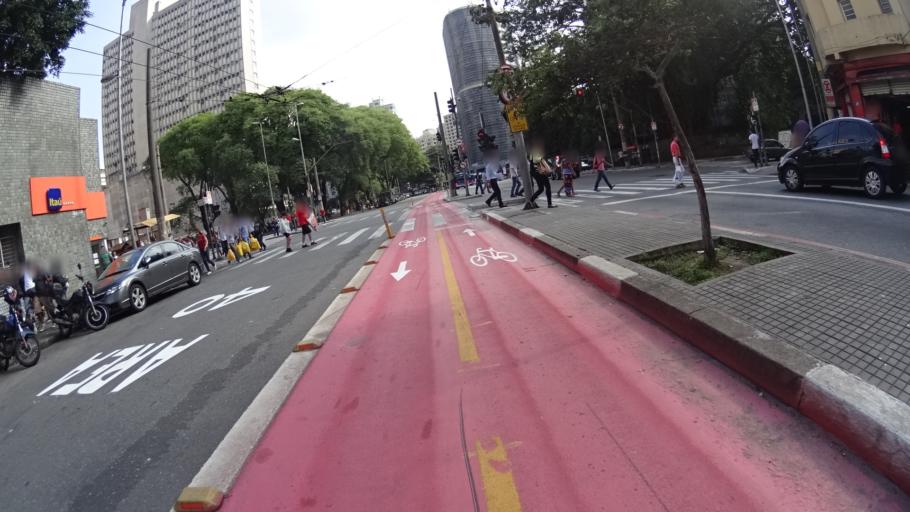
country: BR
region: Sao Paulo
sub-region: Sao Paulo
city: Sao Paulo
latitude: -23.5385
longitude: -46.6359
